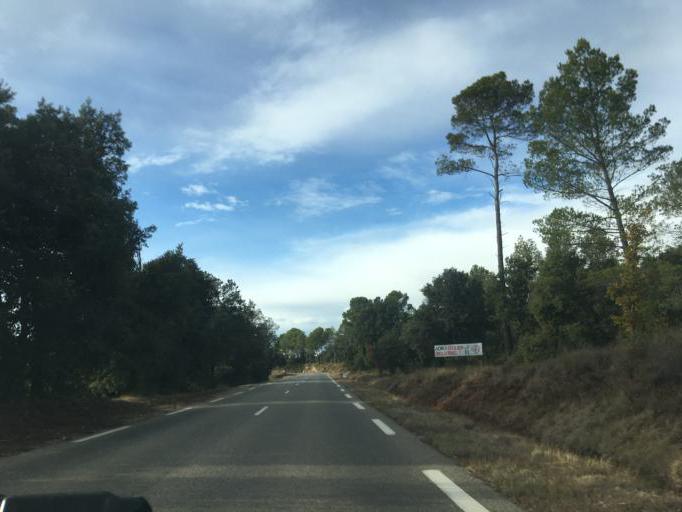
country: FR
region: Provence-Alpes-Cote d'Azur
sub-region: Departement du Var
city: Villecroze
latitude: 43.5950
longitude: 6.2547
